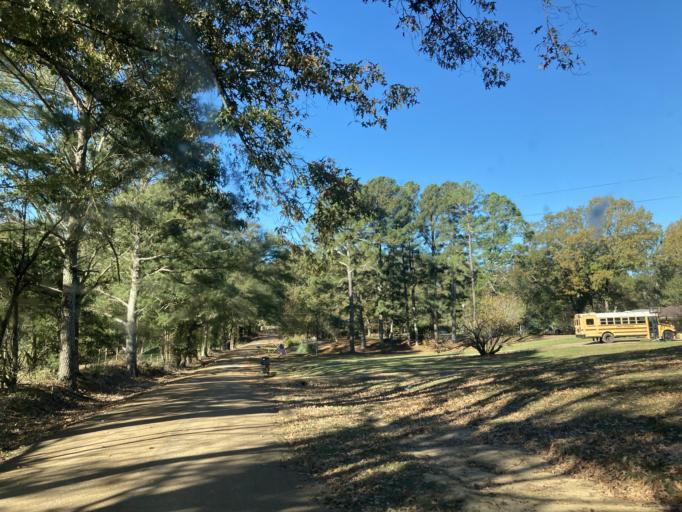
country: US
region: Mississippi
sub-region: Madison County
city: Kearney Park
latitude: 32.7133
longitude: -90.3559
